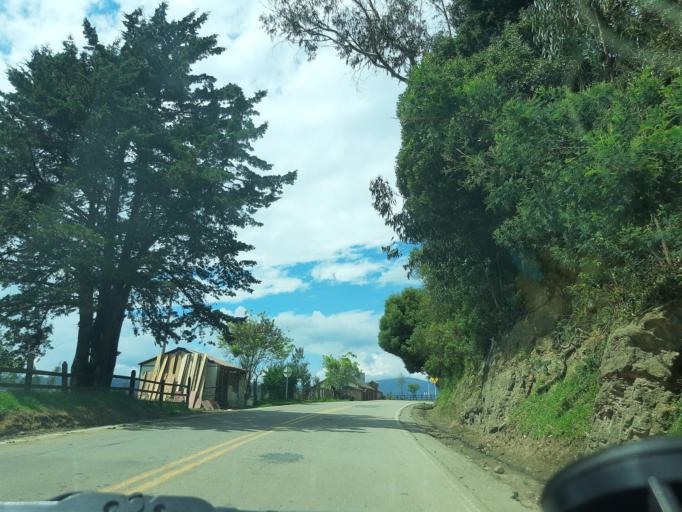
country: CO
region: Boyaca
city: Chiquinquira
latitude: 5.6149
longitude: -73.7447
